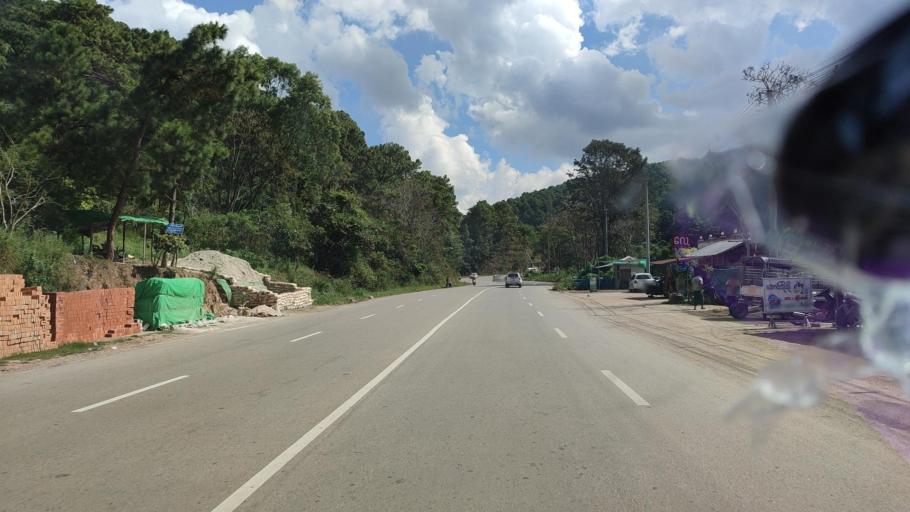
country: MM
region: Mandalay
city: Yamethin
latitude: 20.6323
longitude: 96.5780
